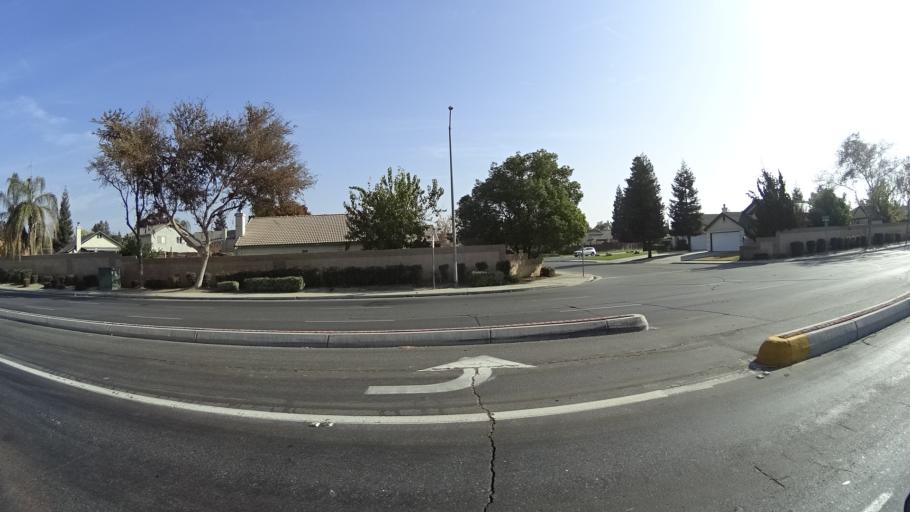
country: US
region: California
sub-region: Kern County
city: Greenacres
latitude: 35.3157
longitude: -119.1095
